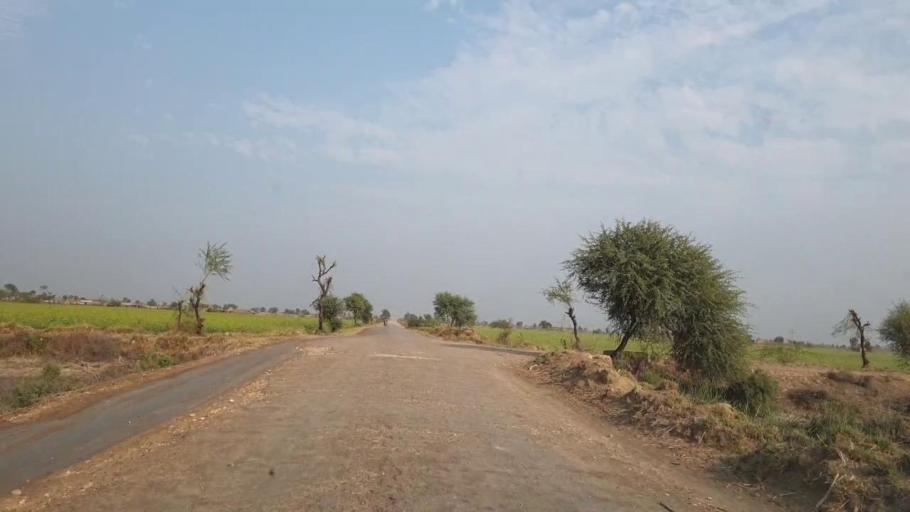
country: PK
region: Sindh
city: Pithoro
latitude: 25.5570
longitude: 69.2041
